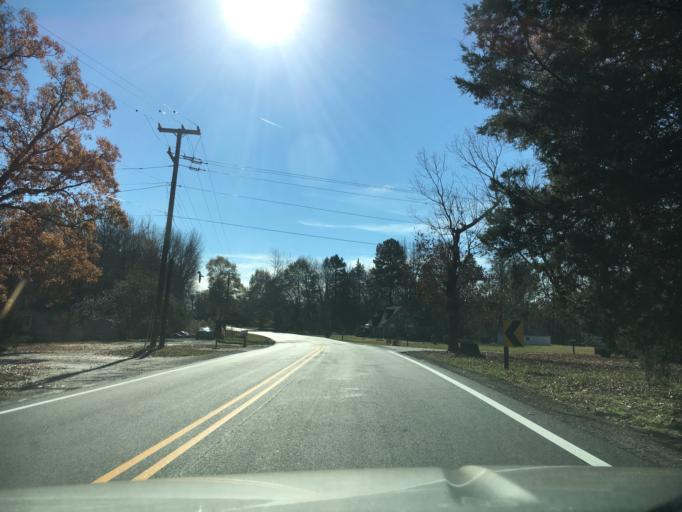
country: US
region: Virginia
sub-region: Cumberland County
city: Cumberland
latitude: 37.4736
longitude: -78.2817
